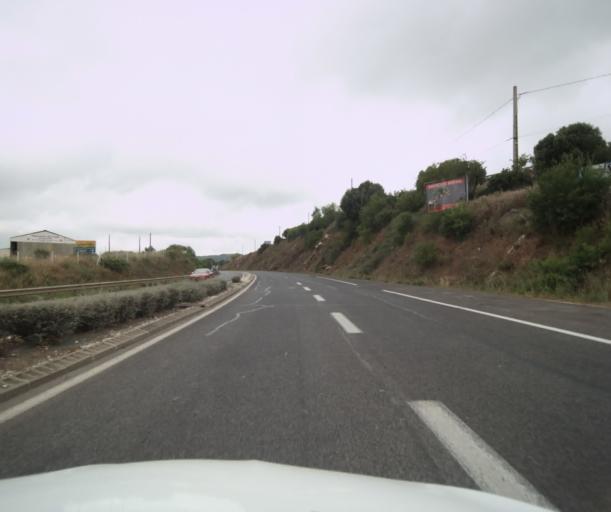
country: FR
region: Provence-Alpes-Cote d'Azur
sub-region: Departement du Var
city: Ollioules
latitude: 43.1217
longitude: 5.8519
